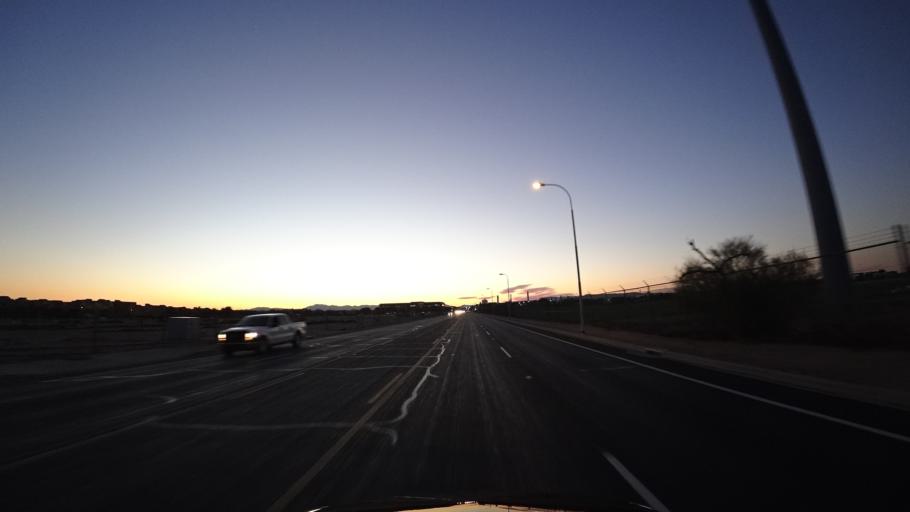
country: US
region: Arizona
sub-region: Maricopa County
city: Chandler
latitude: 33.2987
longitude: -111.8807
